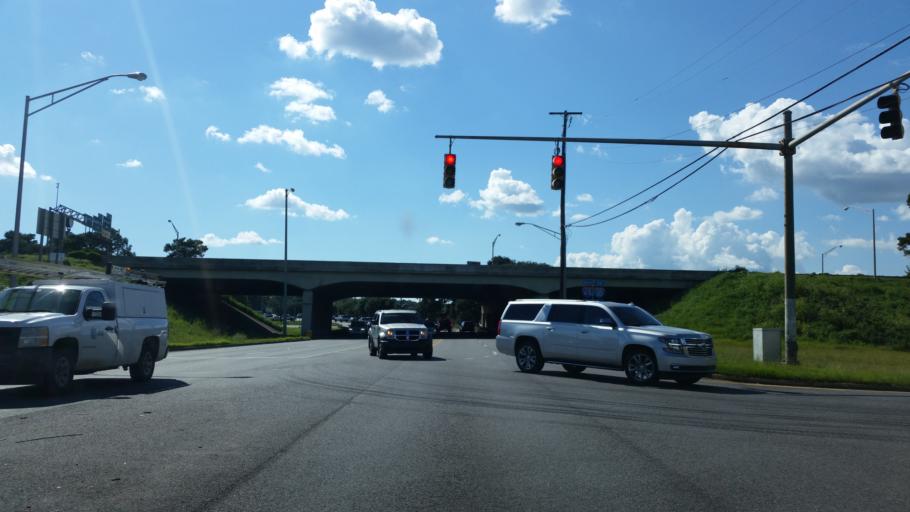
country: US
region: Alabama
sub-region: Mobile County
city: Prichard
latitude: 30.7035
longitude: -88.1222
